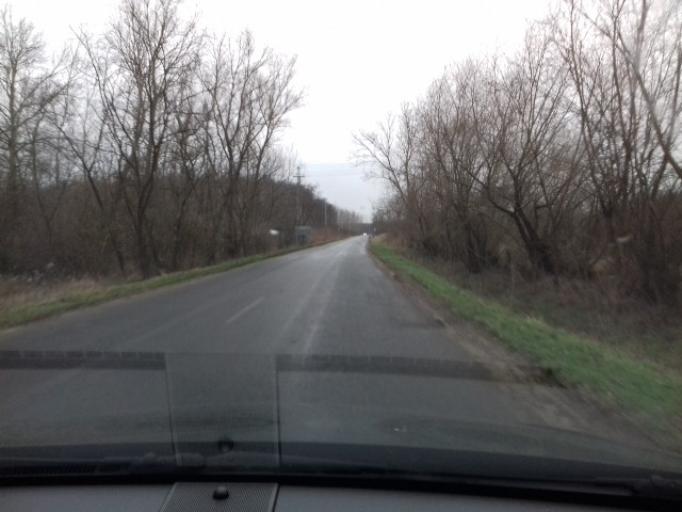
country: HU
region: Szabolcs-Szatmar-Bereg
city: Kek
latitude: 48.0960
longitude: 21.8824
